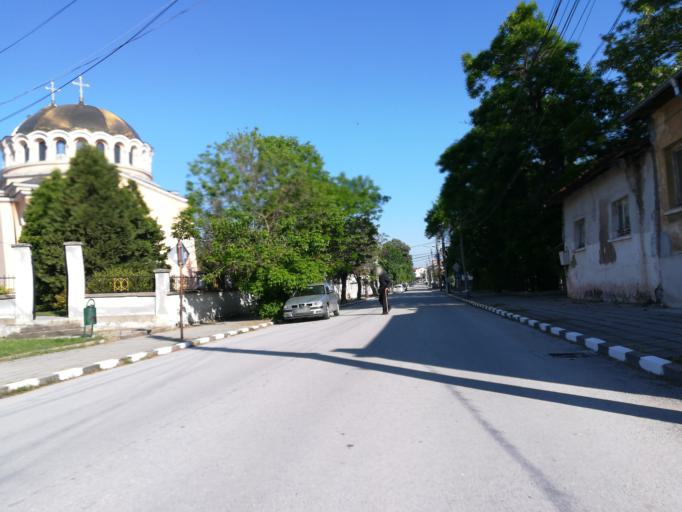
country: BG
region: Stara Zagora
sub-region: Obshtina Chirpan
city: Chirpan
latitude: 42.1018
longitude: 25.2238
